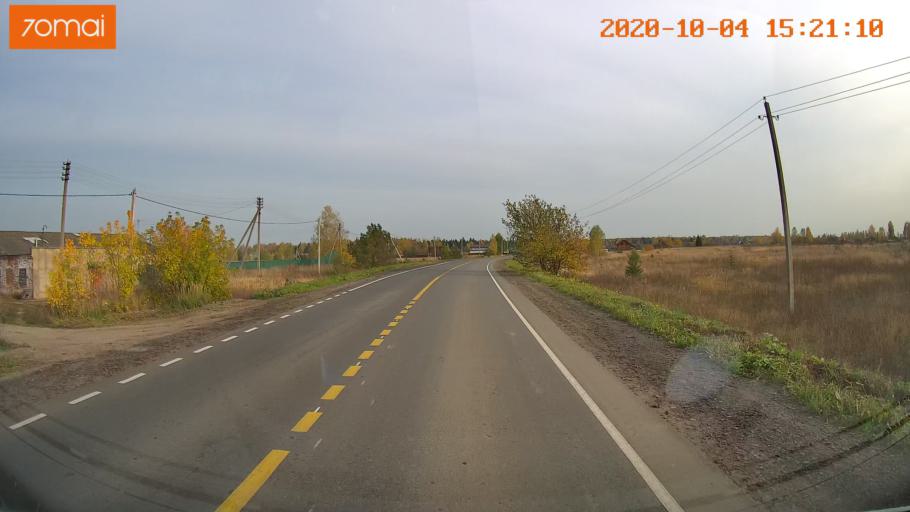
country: RU
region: Ivanovo
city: Bogorodskoye
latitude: 57.0878
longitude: 40.9197
